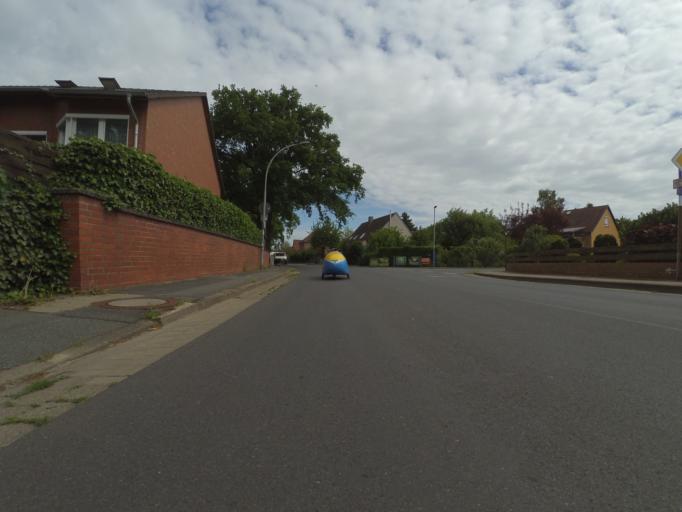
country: DE
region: Lower Saxony
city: Gross Munzel
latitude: 52.4286
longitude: 9.5112
